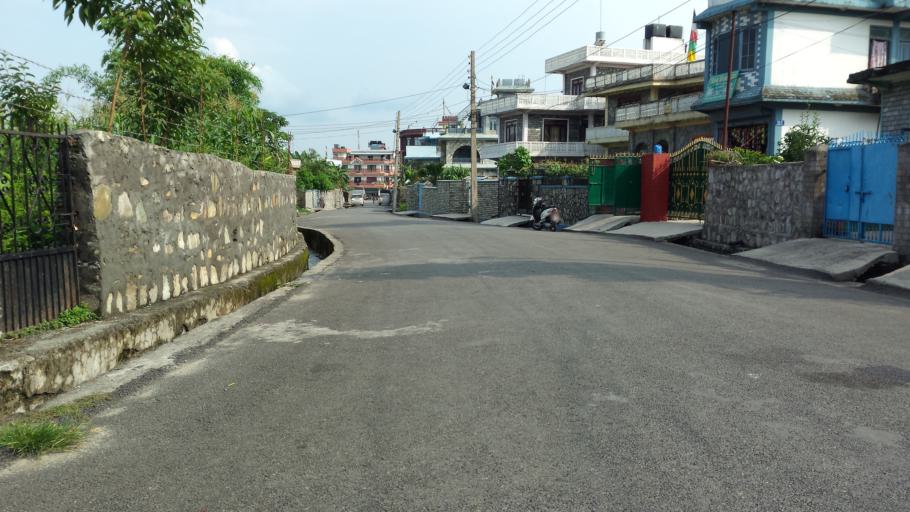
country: NP
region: Western Region
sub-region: Gandaki Zone
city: Pokhara
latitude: 28.2083
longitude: 83.9990
